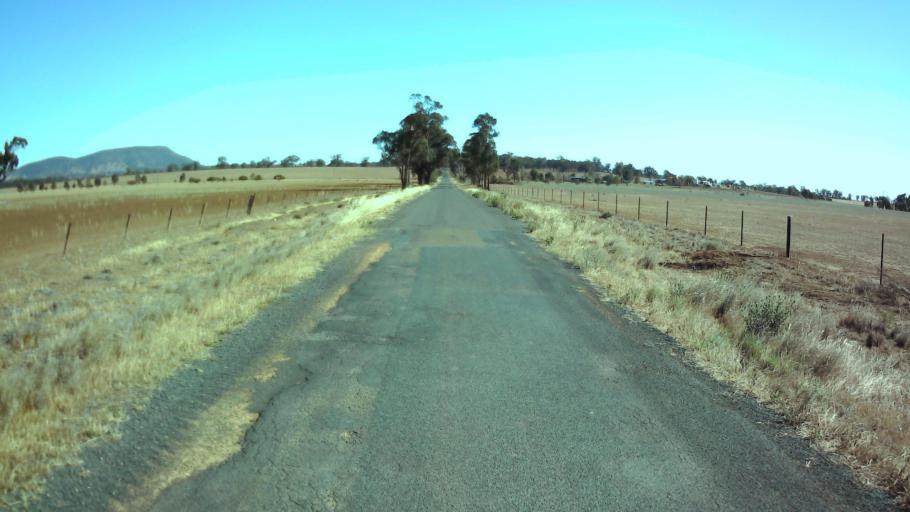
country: AU
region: New South Wales
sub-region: Weddin
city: Grenfell
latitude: -33.7973
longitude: 147.9564
